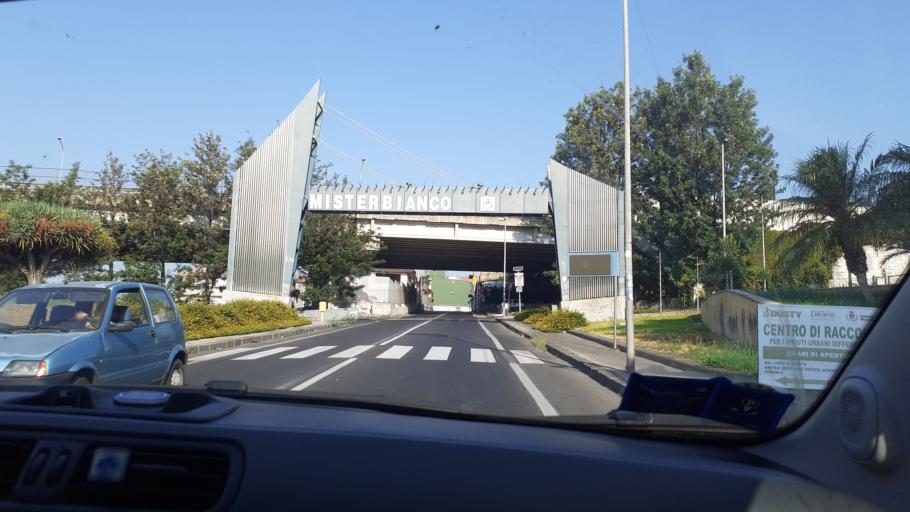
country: IT
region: Sicily
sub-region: Catania
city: Misterbianco
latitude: 37.5157
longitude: 15.0208
